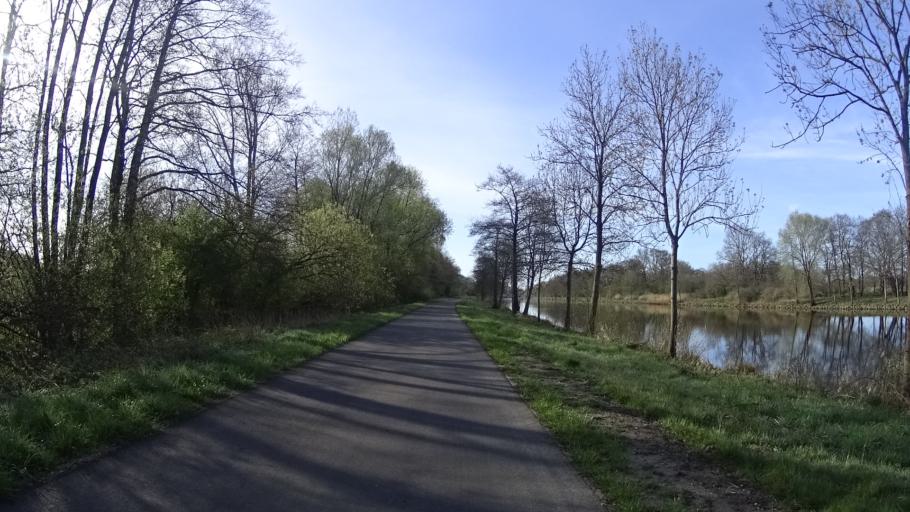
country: DE
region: Lower Saxony
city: Haren
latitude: 52.8047
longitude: 7.2600
